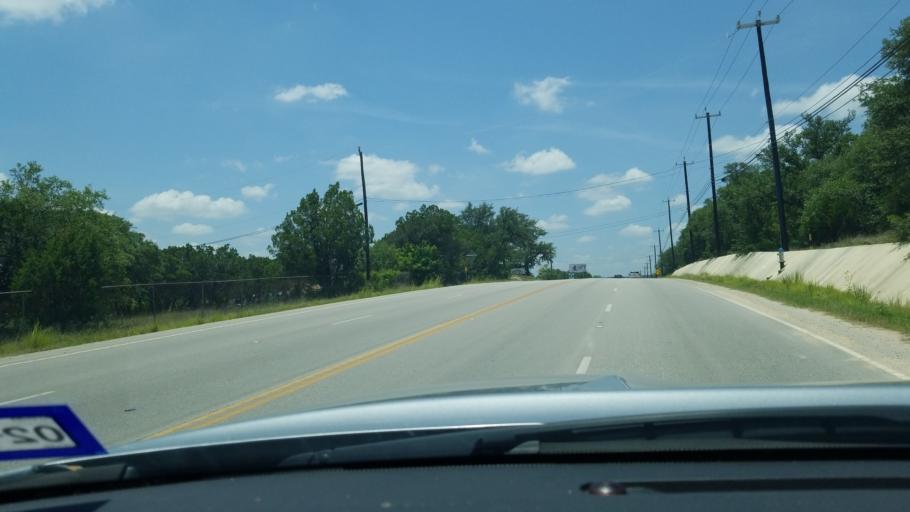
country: US
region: Texas
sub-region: Bexar County
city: Timberwood Park
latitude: 29.7151
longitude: -98.4735
